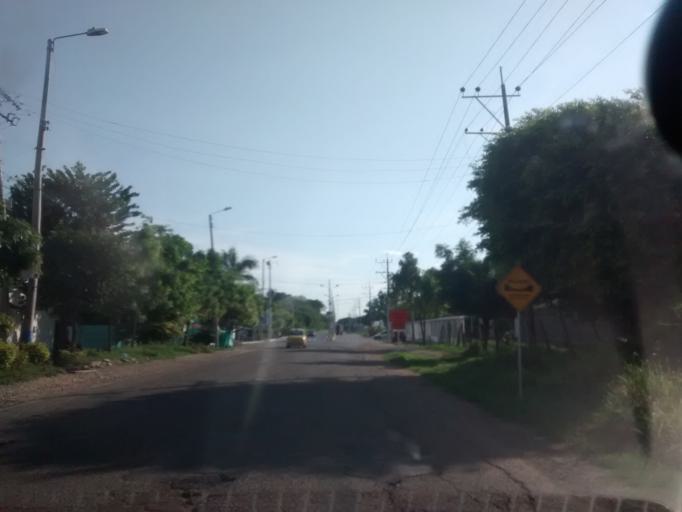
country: CO
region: Cundinamarca
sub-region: Girardot
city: Girardot City
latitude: 4.3110
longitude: -74.8100
